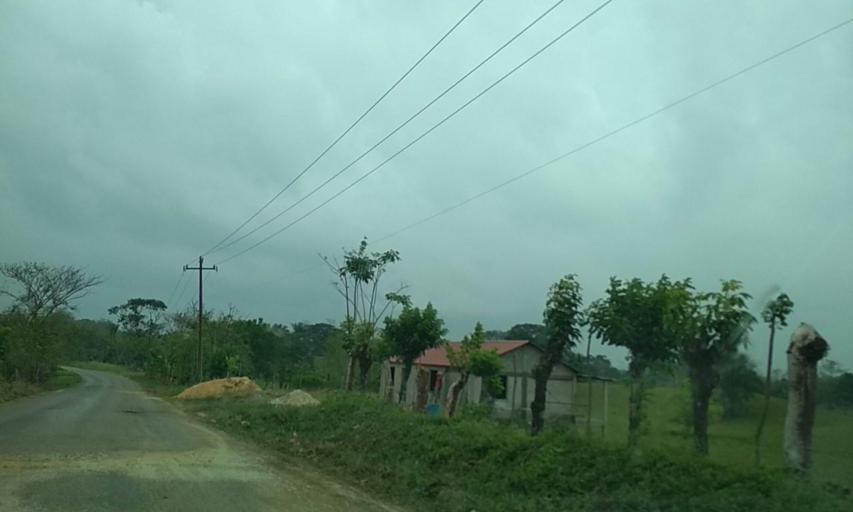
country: MX
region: Tabasco
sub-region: Huimanguillo
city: Francisco Rueda
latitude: 17.5832
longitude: -94.0923
